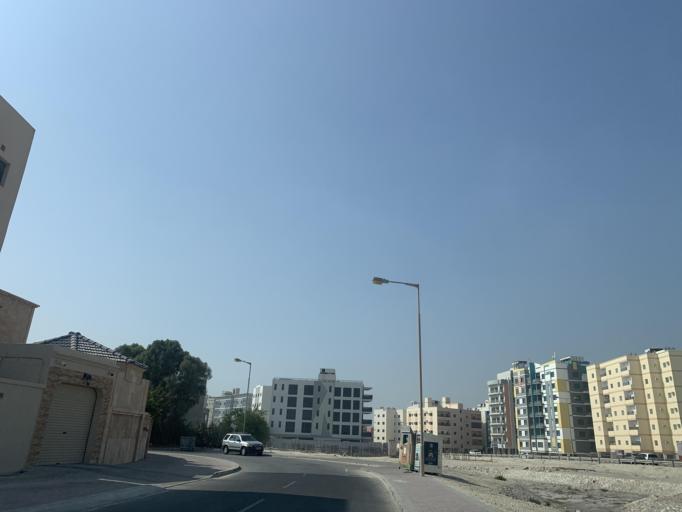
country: BH
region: Central Governorate
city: Madinat Hamad
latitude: 26.1298
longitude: 50.4912
